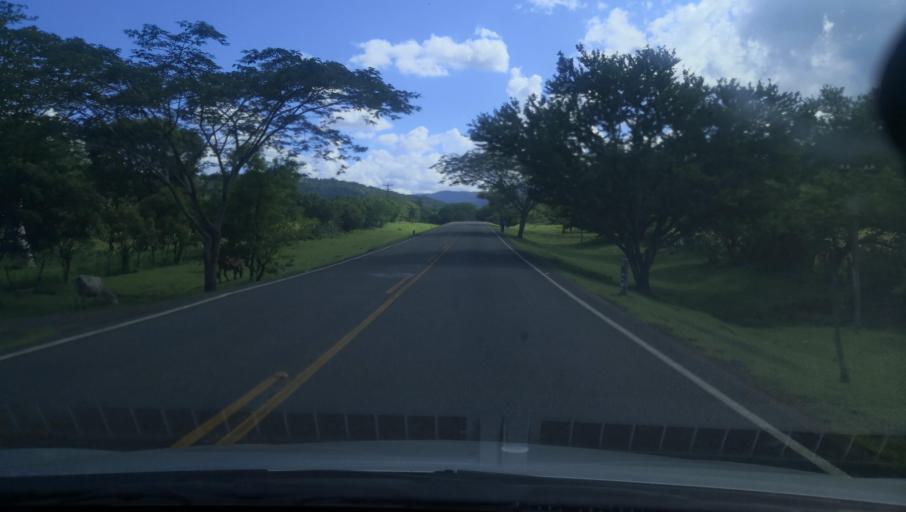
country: NI
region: Madriz
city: Somoto
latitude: 13.4599
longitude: -86.6649
